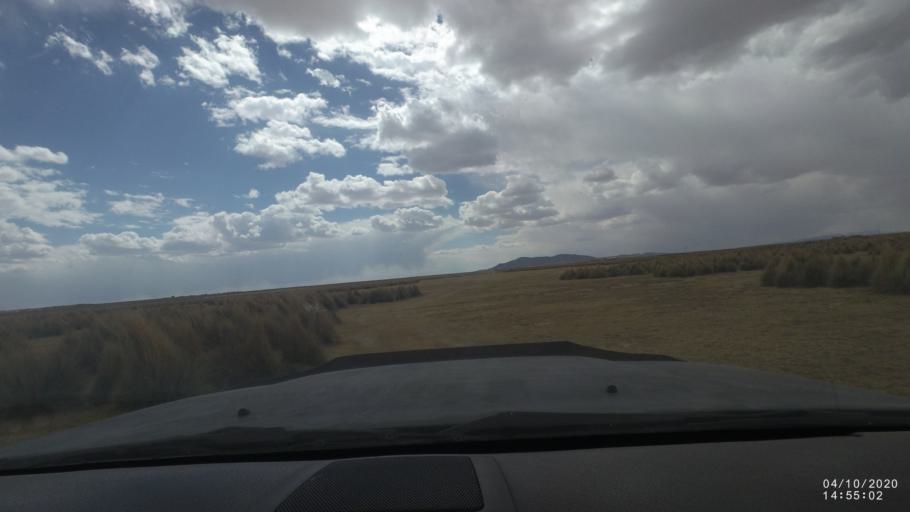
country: BO
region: Oruro
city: Poopo
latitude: -18.6854
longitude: -67.5109
